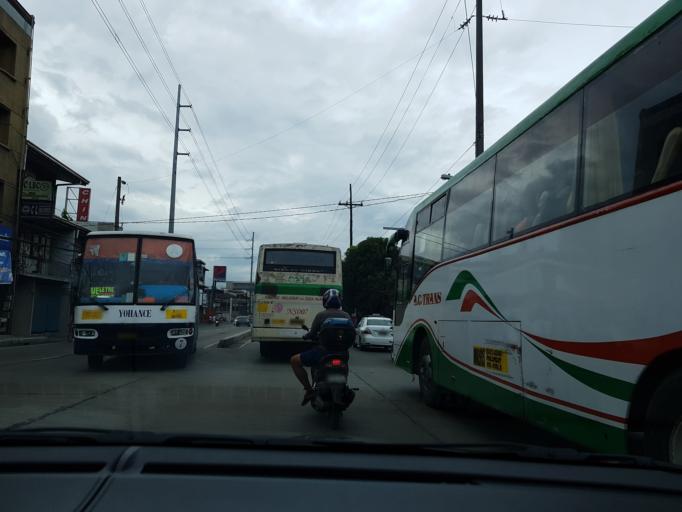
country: PH
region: Metro Manila
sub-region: Caloocan City
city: Niugan
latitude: 14.6637
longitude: 120.9842
